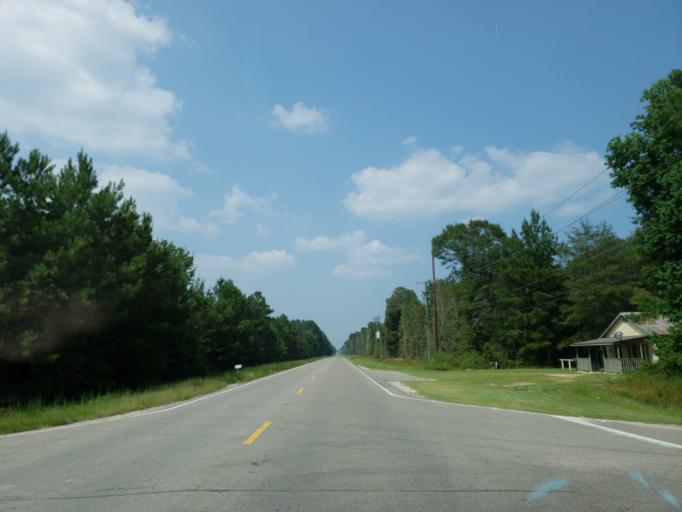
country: US
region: Mississippi
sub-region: Forrest County
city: Glendale
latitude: 31.4556
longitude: -89.2853
